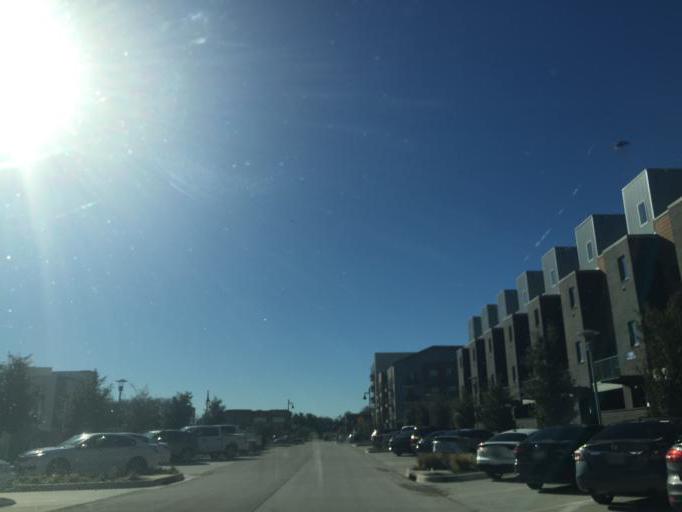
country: US
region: Texas
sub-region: Tarrant County
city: Fort Worth
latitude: 32.7539
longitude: -97.3490
